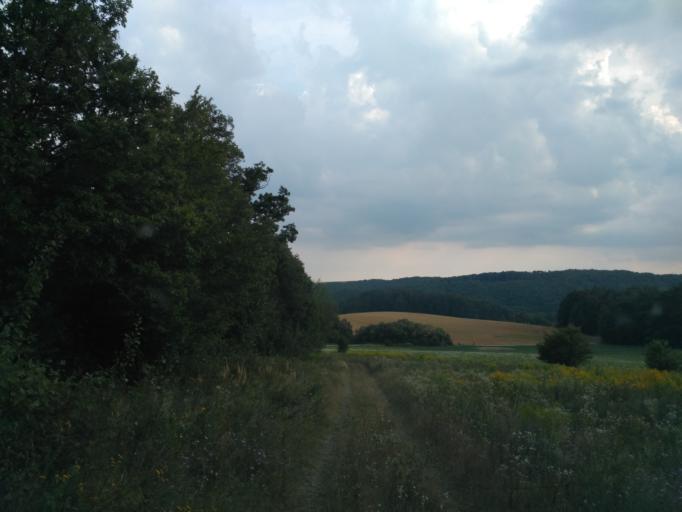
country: SK
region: Kosicky
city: Kosice
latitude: 48.7339
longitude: 21.1672
